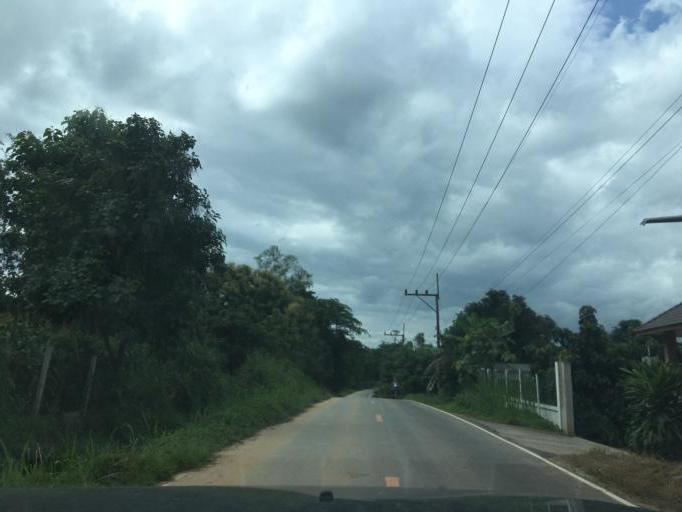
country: TH
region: Chiang Rai
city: Wiang Pa Pao
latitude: 19.2317
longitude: 99.4911
